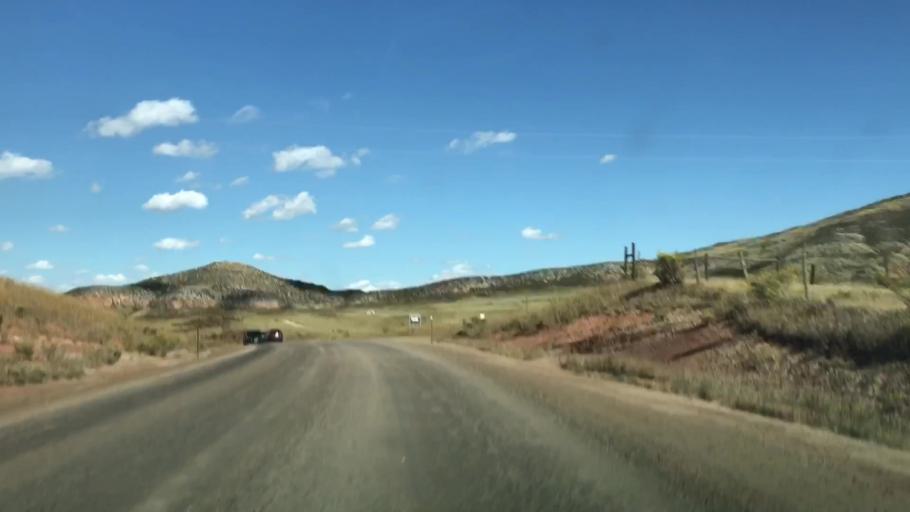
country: US
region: Colorado
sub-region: Larimer County
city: Laporte
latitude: 40.7655
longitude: -105.1697
